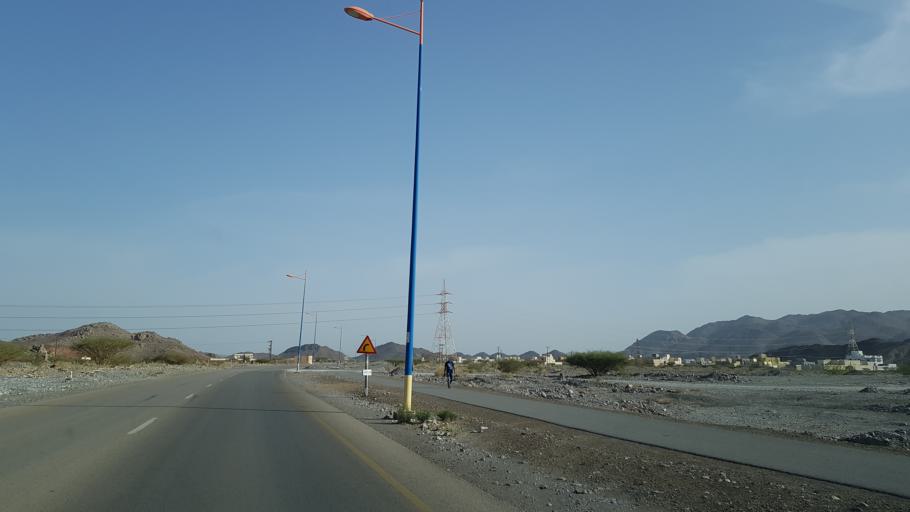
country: OM
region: Muhafazat ad Dakhiliyah
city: Izki
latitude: 22.9098
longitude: 57.6758
